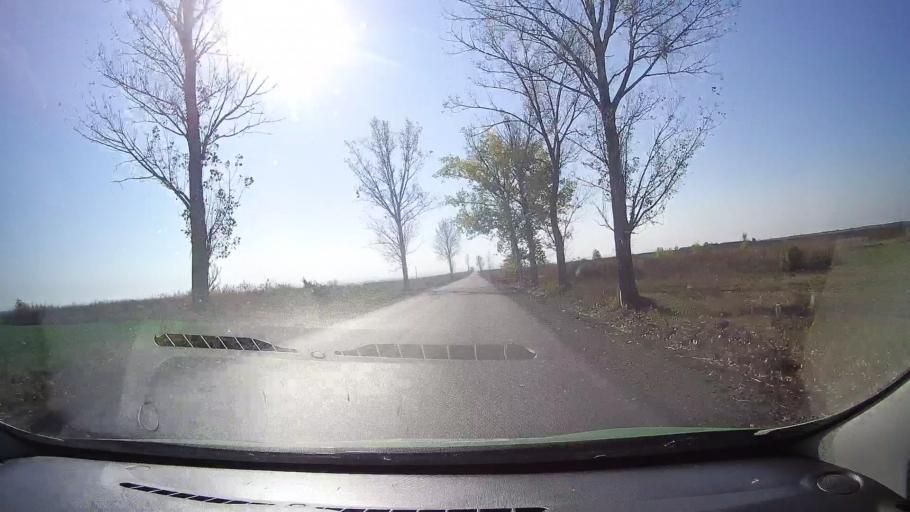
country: RO
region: Satu Mare
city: Carei
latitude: 47.6507
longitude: 22.4622
